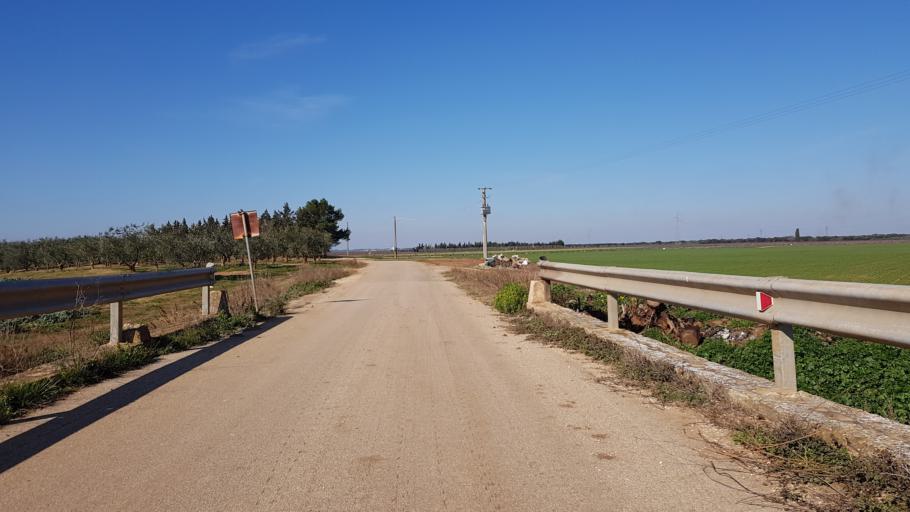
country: IT
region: Apulia
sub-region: Provincia di Brindisi
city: Mesagne
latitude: 40.6196
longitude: 17.8149
